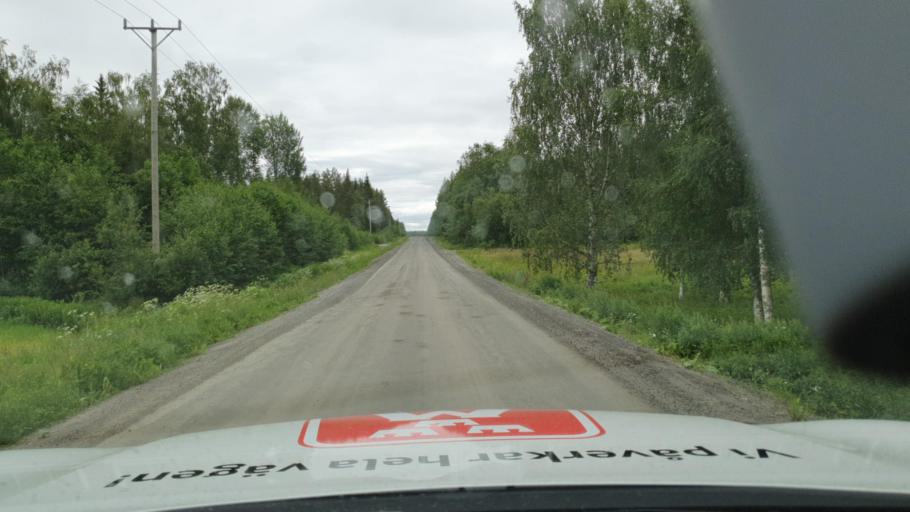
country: SE
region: Vaesterbotten
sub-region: Nordmalings Kommun
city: Nordmaling
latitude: 63.6506
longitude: 19.4364
